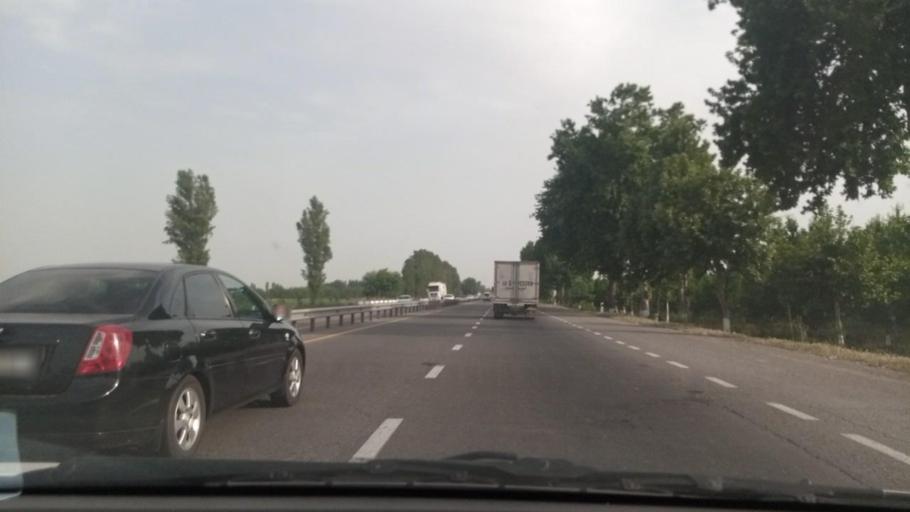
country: UZ
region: Toshkent Shahri
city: Bektemir
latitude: 41.2161
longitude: 69.4025
